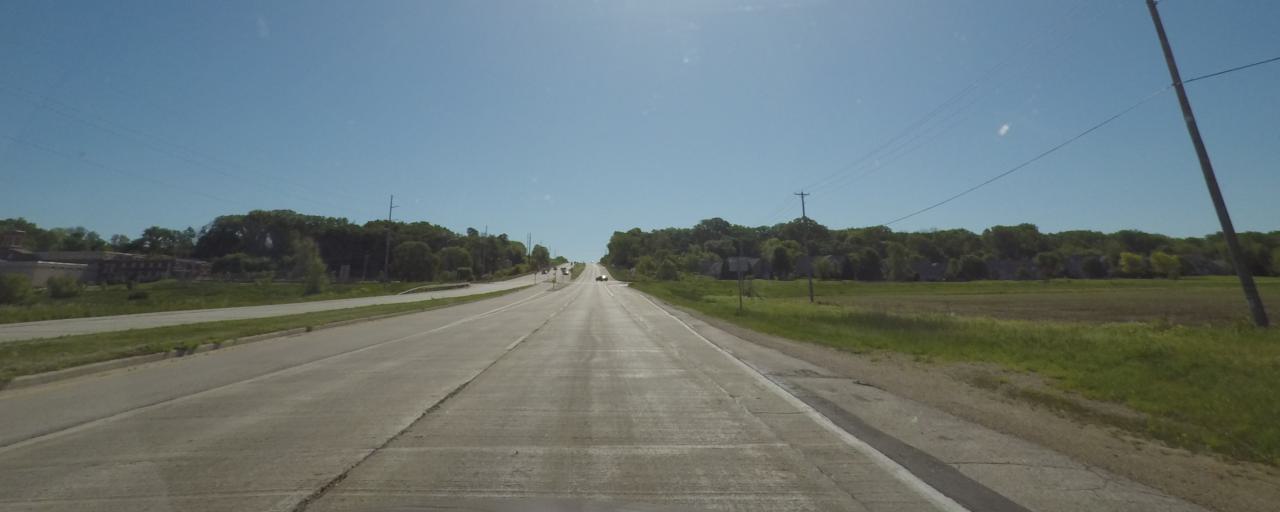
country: US
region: Wisconsin
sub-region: Fond du Lac County
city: Fond du Lac
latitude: 43.7836
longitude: -88.3887
